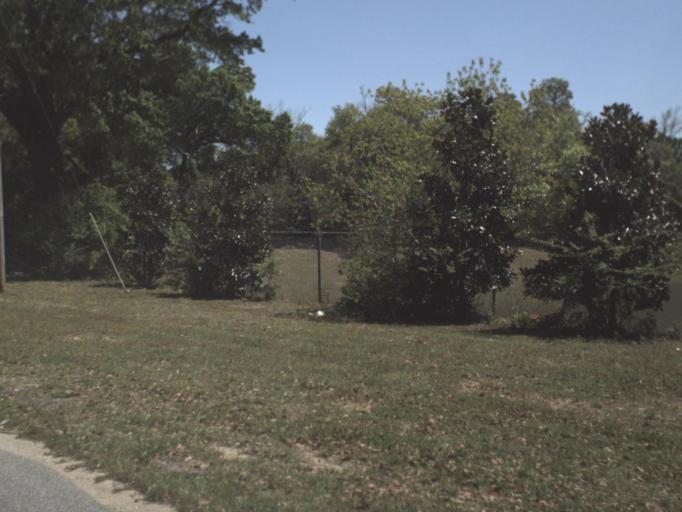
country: US
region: Florida
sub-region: Escambia County
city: Bellview
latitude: 30.4615
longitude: -87.3177
